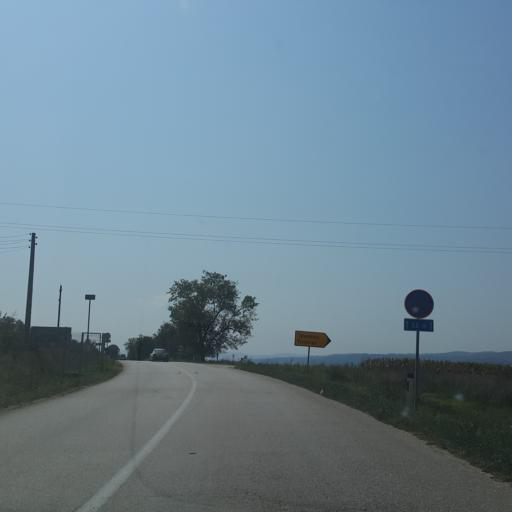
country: RS
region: Central Serbia
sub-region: Zajecarski Okrug
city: Knjazevac
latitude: 43.6780
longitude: 22.2896
